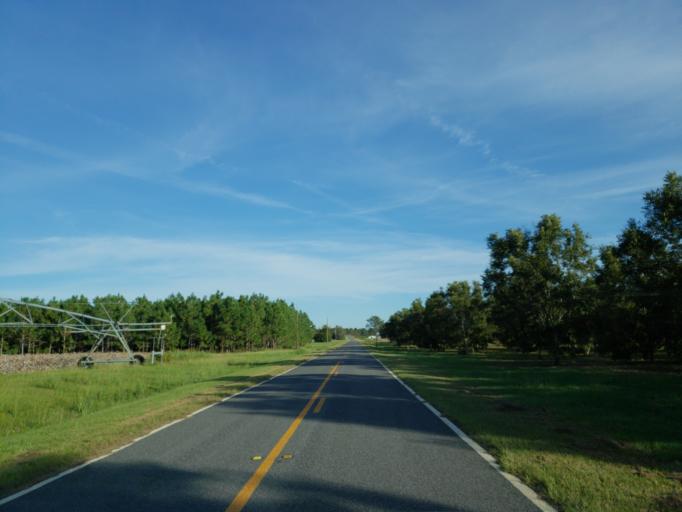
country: US
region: Georgia
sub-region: Dooly County
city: Vienna
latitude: 32.0632
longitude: -83.7704
